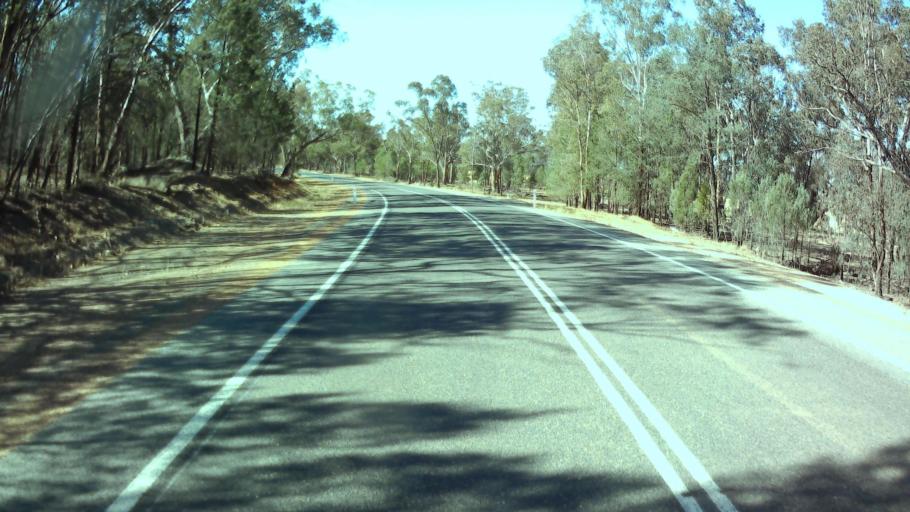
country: AU
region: New South Wales
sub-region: Weddin
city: Grenfell
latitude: -33.7450
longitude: 148.0883
